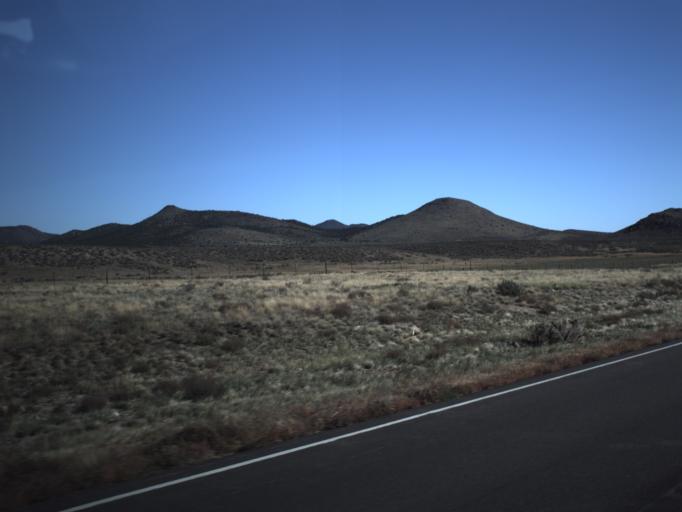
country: US
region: Utah
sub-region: Washington County
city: Enterprise
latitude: 37.7853
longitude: -113.9602
